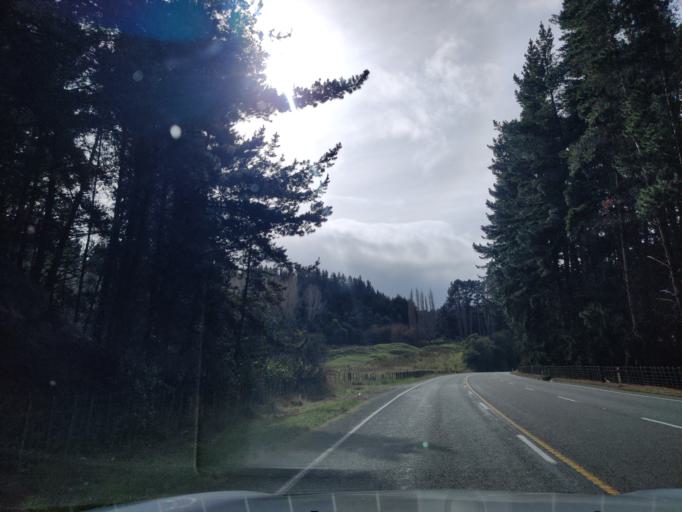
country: NZ
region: Manawatu-Wanganui
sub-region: Ruapehu District
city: Waiouru
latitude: -39.7609
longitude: 175.8048
